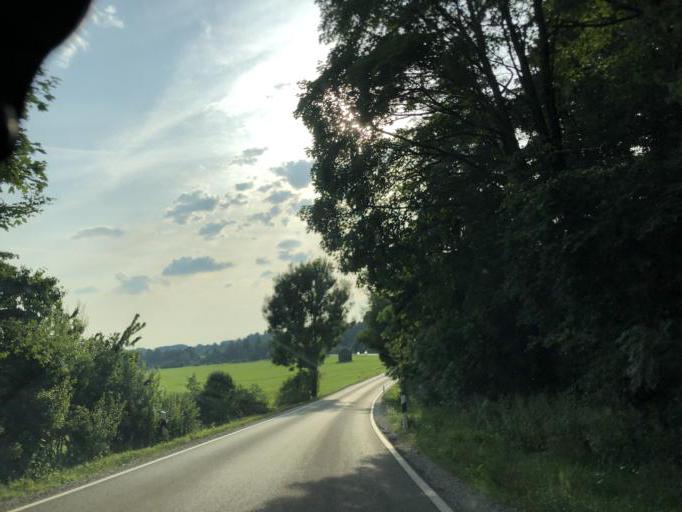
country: DE
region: Bavaria
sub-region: Swabia
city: Wald
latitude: 47.7559
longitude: 10.5458
